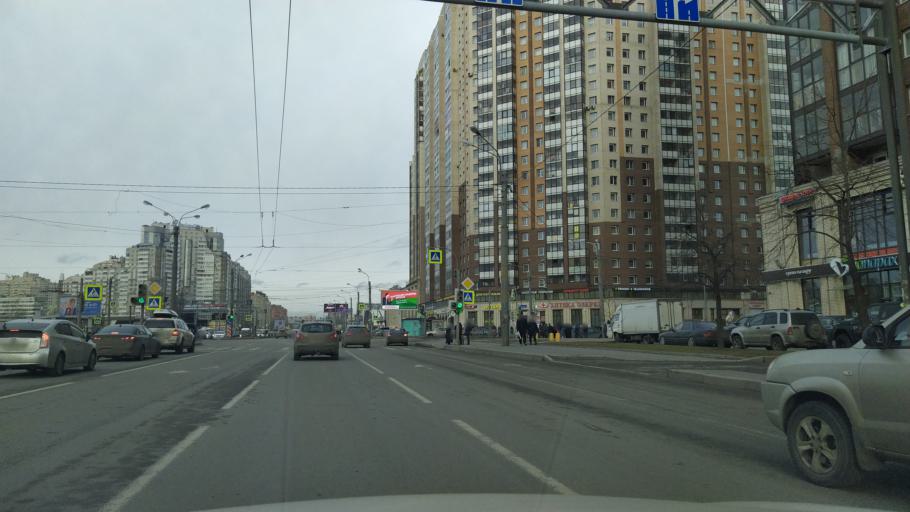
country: RU
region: Leningrad
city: Chernaya Rechka
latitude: 59.9999
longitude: 30.2992
